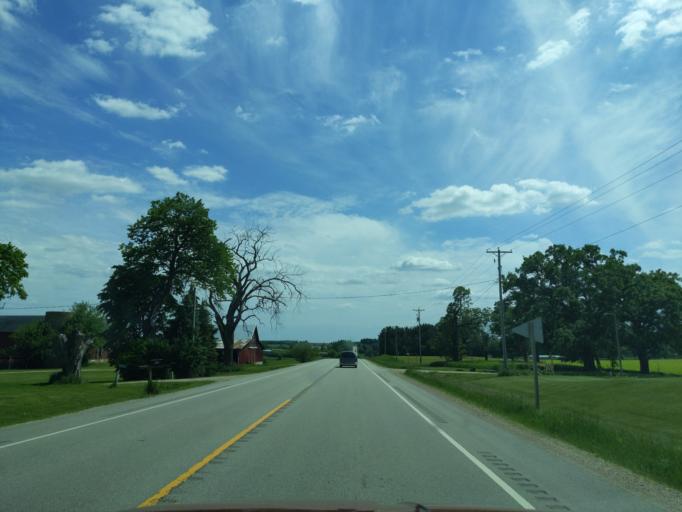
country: US
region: Wisconsin
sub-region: Columbia County
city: Poynette
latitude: 43.3942
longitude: -89.3277
